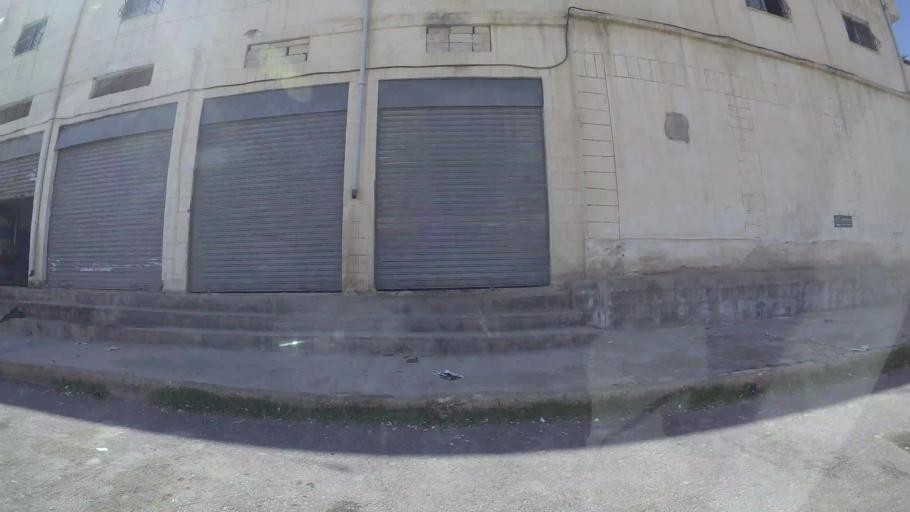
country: JO
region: Amman
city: Al Bunayyat ash Shamaliyah
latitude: 31.9044
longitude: 35.8998
